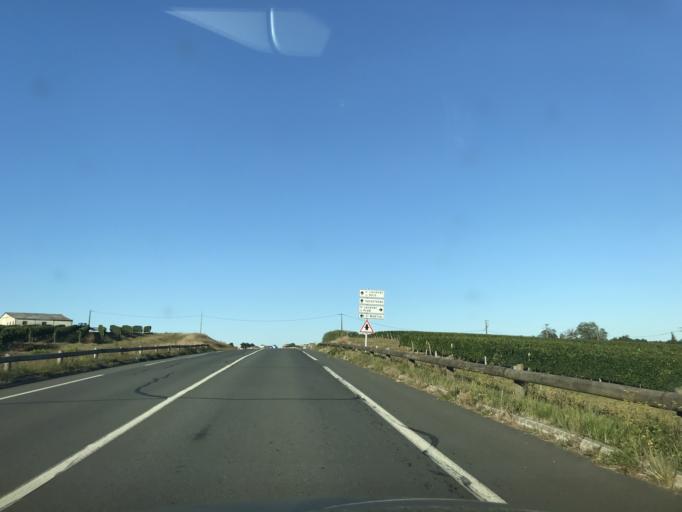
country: FR
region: Aquitaine
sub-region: Departement de la Gironde
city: Castets-en-Dorthe
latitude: 44.6272
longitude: -0.1466
